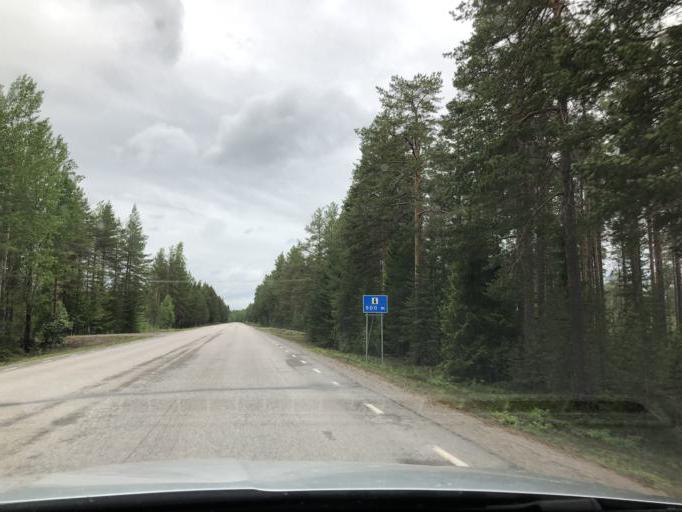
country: SE
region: Norrbotten
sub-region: Pitea Kommun
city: Bergsviken
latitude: 65.3764
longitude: 21.3474
